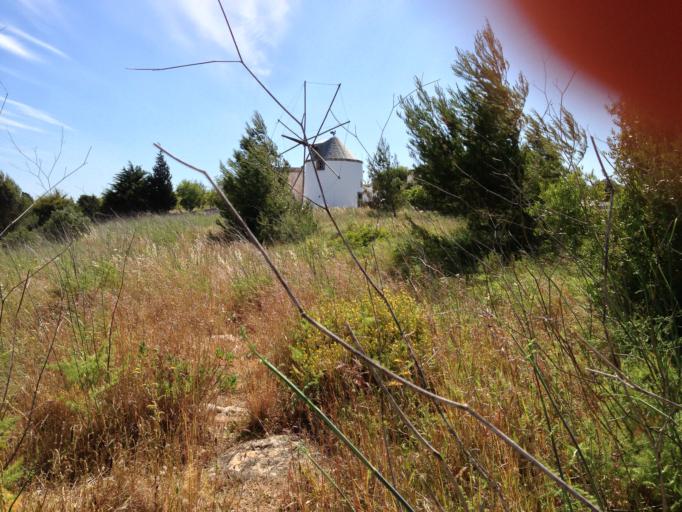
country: PT
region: Setubal
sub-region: Setubal
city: Setubal
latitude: 38.5203
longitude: -8.9122
